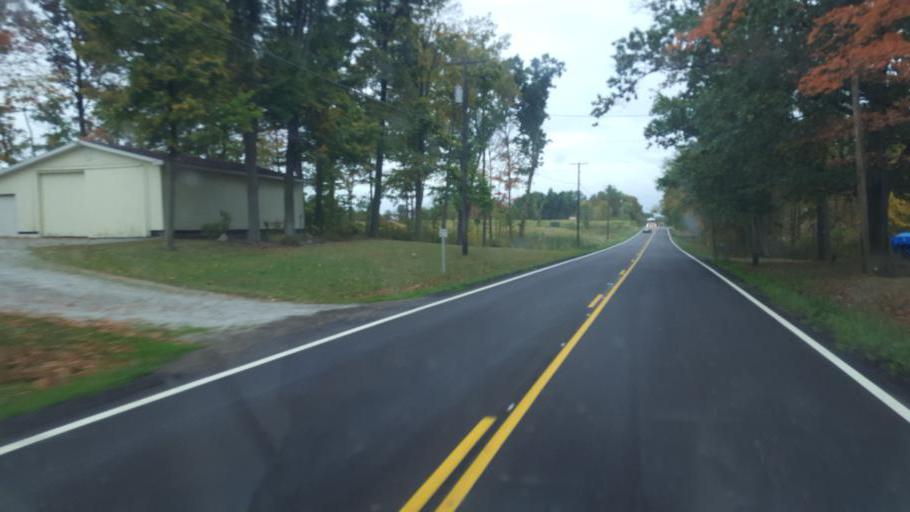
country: US
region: Ohio
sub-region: Huron County
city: New London
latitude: 40.9844
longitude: -82.3702
